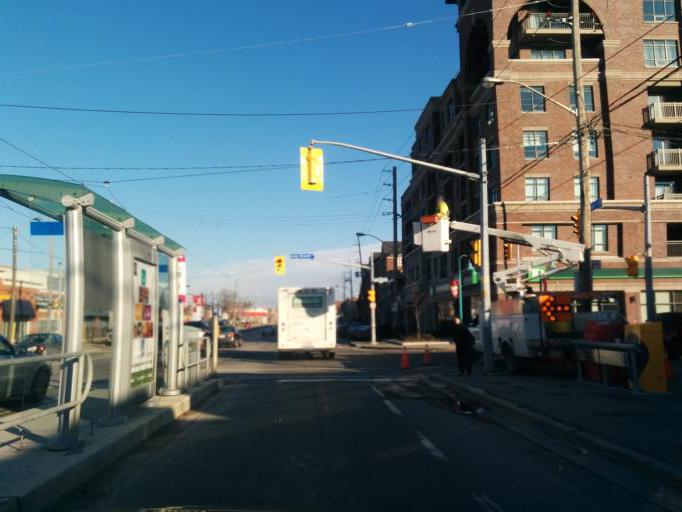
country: CA
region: Ontario
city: Etobicoke
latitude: 43.5943
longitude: -79.5343
